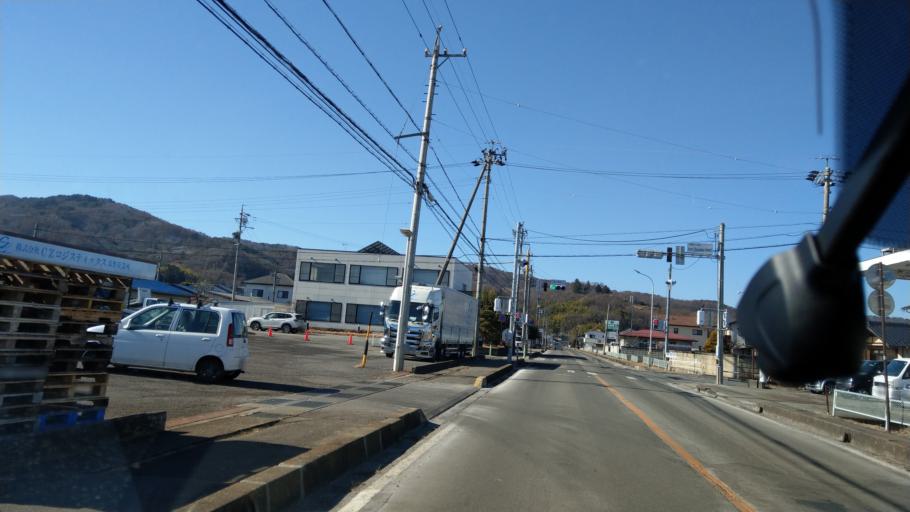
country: JP
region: Nagano
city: Saku
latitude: 36.2253
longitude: 138.4509
